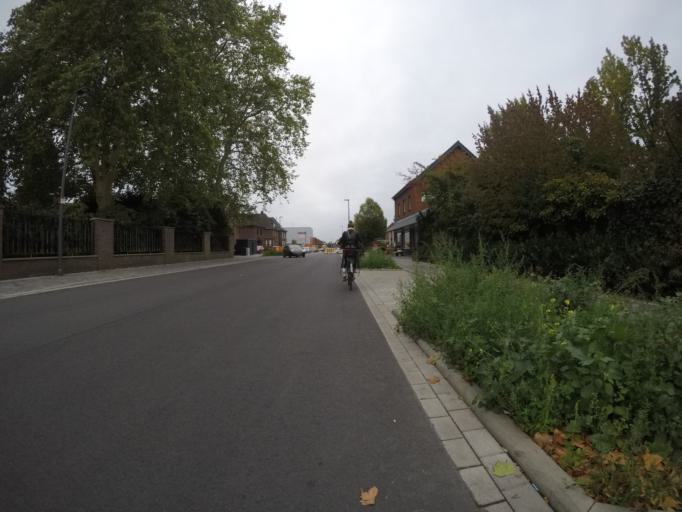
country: DE
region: North Rhine-Westphalia
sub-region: Regierungsbezirk Munster
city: Rhede
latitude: 51.8382
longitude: 6.6921
